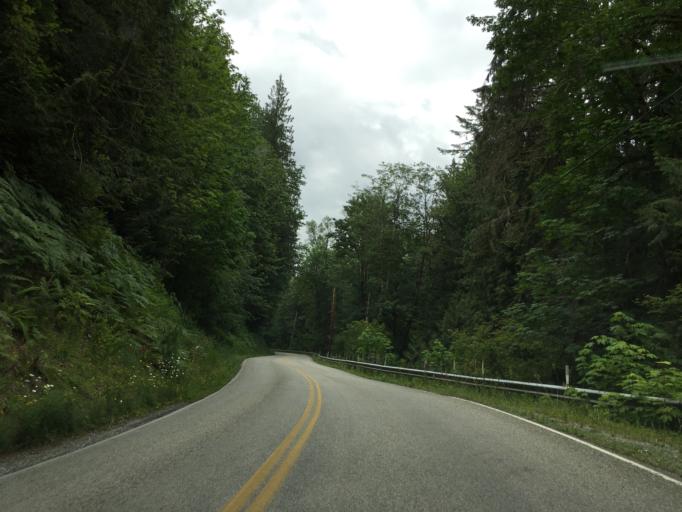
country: US
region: Washington
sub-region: Whatcom County
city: Peaceful Valley
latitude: 48.9343
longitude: -122.0690
